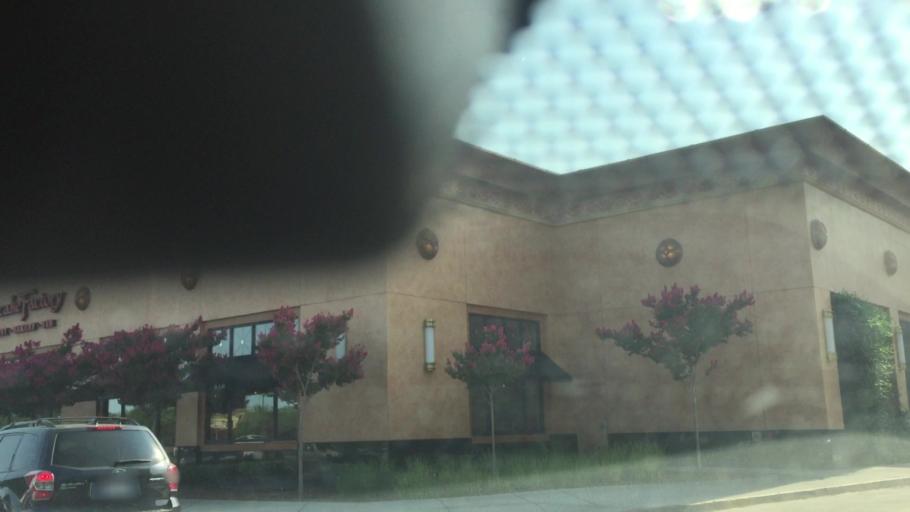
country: US
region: California
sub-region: Placer County
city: Roseville
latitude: 38.7732
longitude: -121.2683
